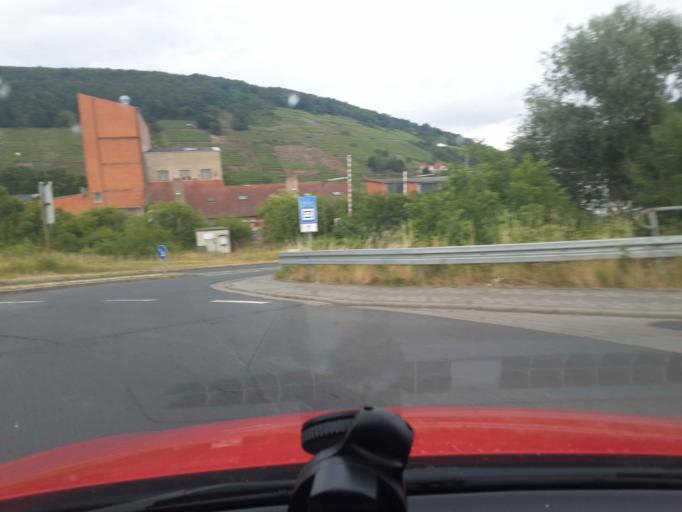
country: DE
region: Bavaria
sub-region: Regierungsbezirk Unterfranken
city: Klingenberg am Main
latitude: 49.7843
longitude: 9.1738
